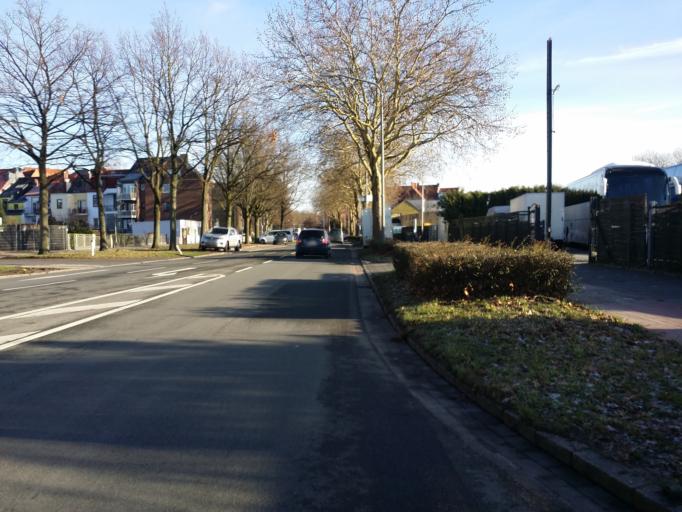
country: DE
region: Bremen
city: Bremen
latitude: 53.0758
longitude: 8.7805
